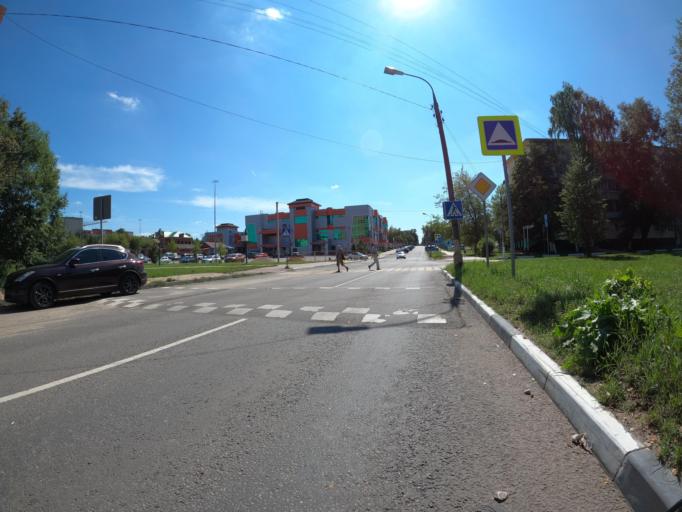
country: RU
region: Moskovskaya
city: Stupino
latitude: 54.8915
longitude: 38.0853
